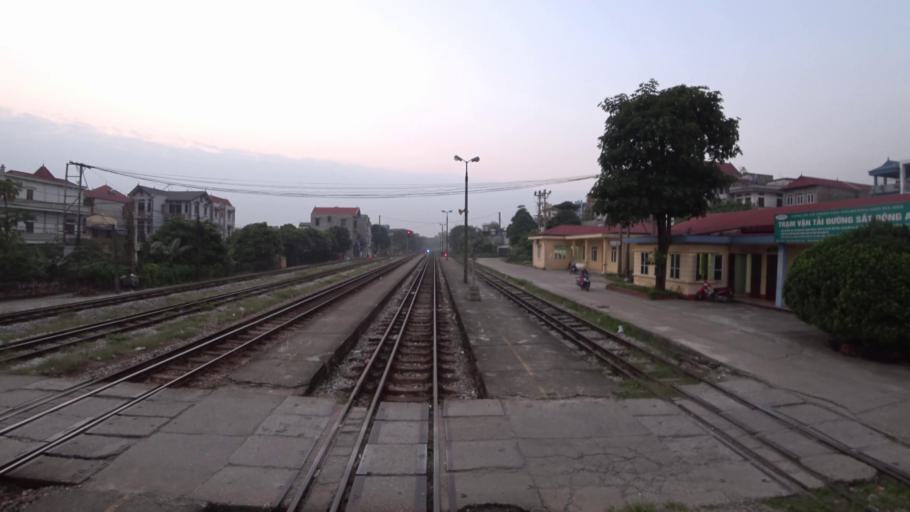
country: VN
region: Ha Noi
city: Soc Son
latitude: 21.2210
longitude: 105.8599
